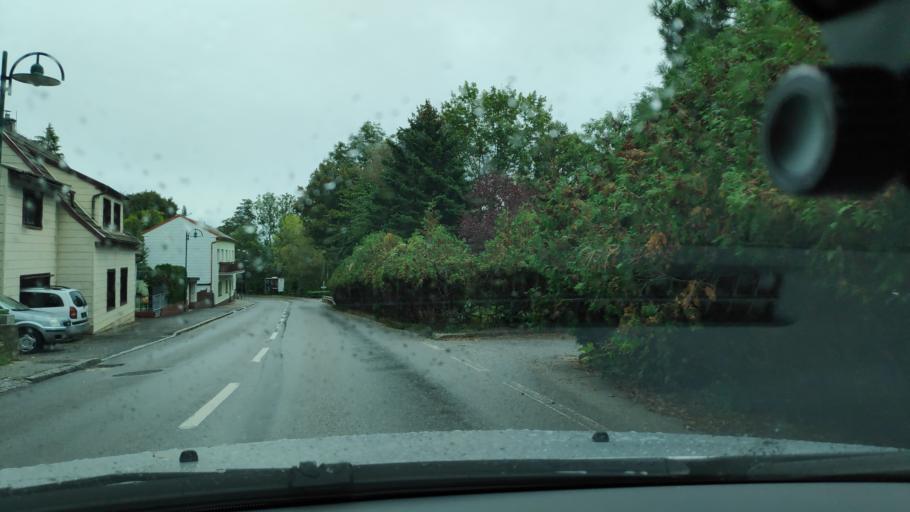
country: AT
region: Lower Austria
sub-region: Politischer Bezirk Neunkirchen
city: Willendorf am Steinfelde
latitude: 47.7912
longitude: 16.0454
